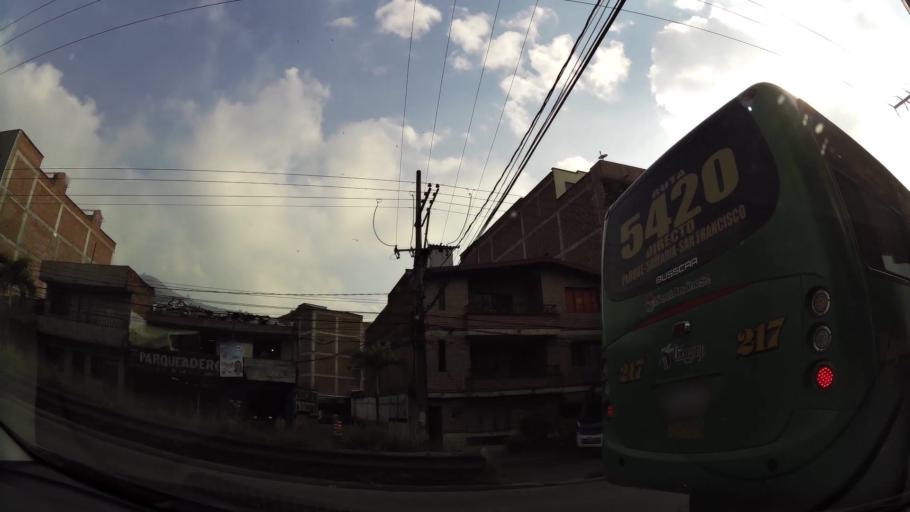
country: CO
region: Antioquia
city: Sabaneta
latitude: 6.1689
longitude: -75.6237
